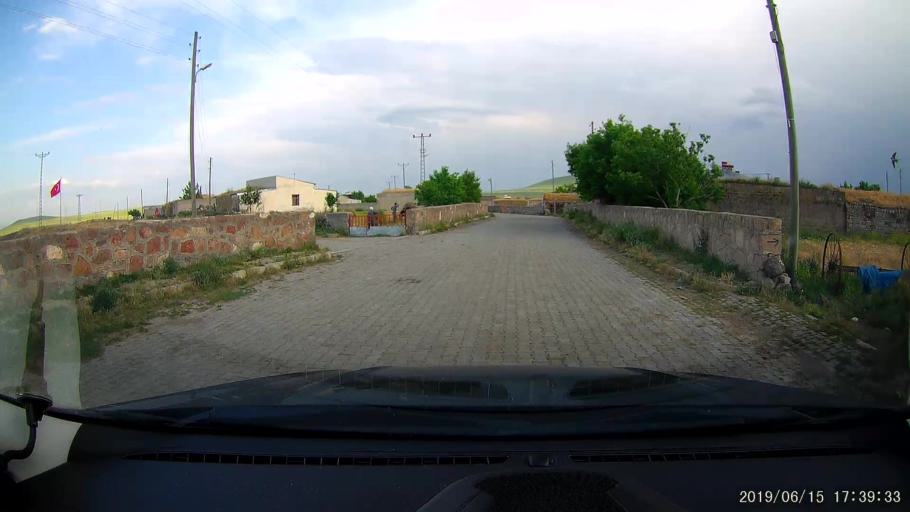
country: TR
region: Kars
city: Basgedikler
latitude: 40.5154
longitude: 43.5707
